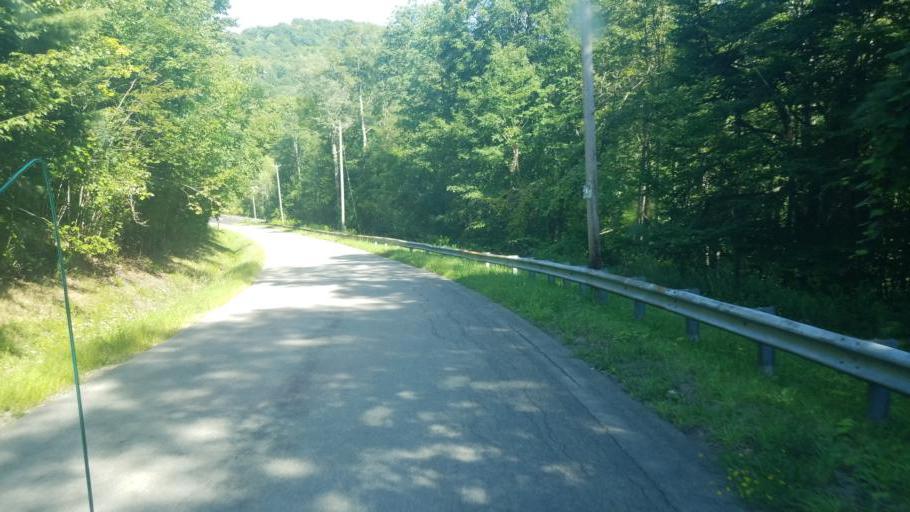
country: US
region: New York
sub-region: Allegany County
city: Wellsville
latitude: 42.0581
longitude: -78.0458
